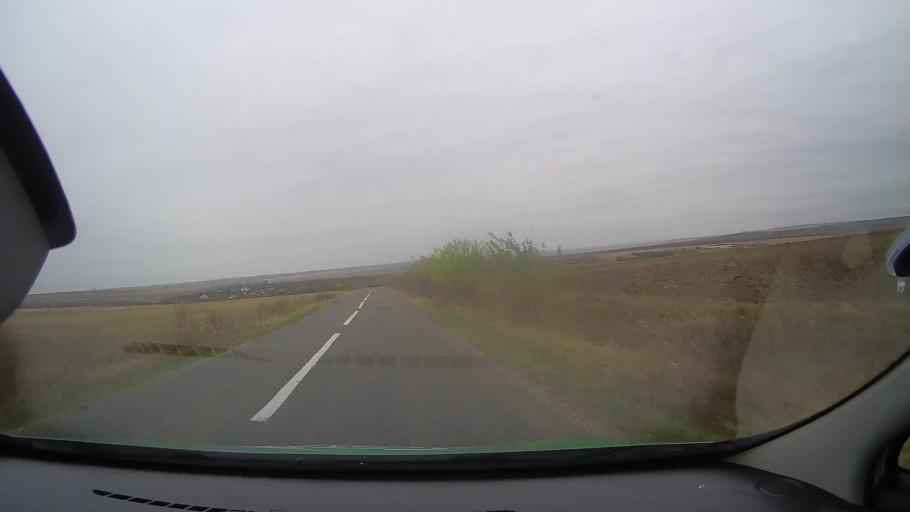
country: RO
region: Constanta
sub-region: Comuna Vulturu
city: Vulturu
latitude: 44.6934
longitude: 28.2424
